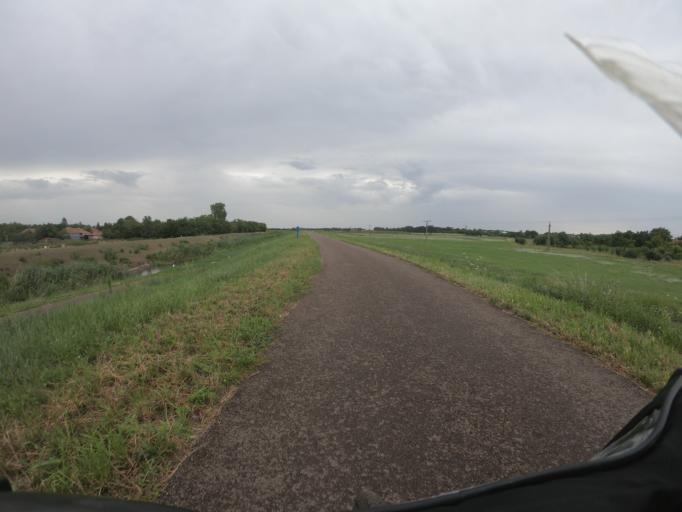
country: HU
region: Heves
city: Poroszlo
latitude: 47.7054
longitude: 20.6580
